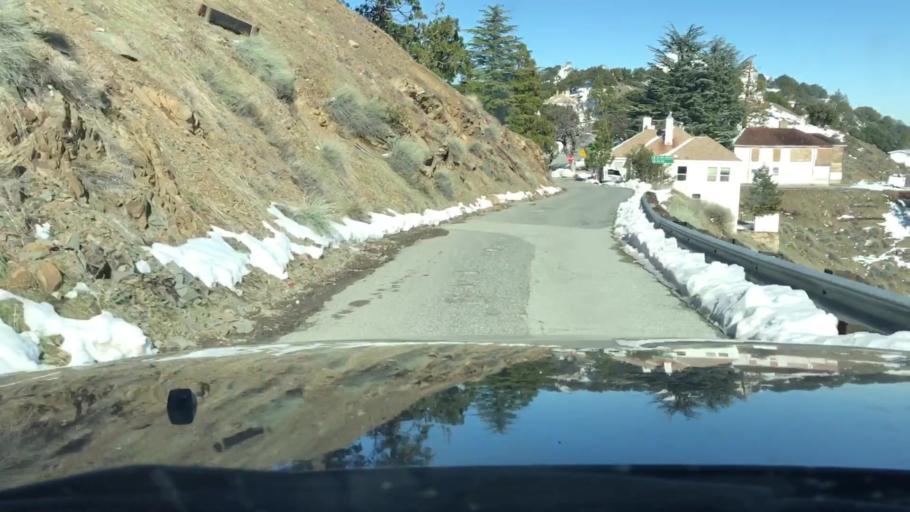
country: US
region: California
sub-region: Santa Clara County
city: East Foothills
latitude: 37.3414
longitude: -121.6421
